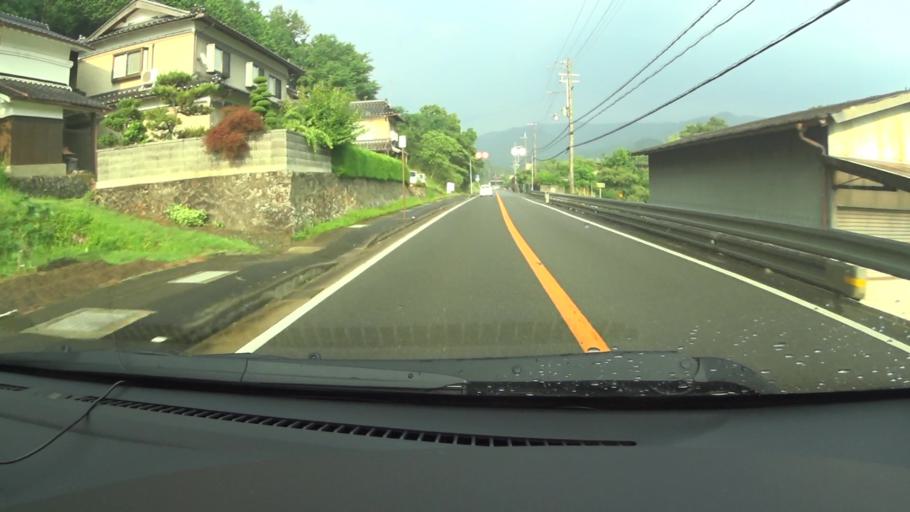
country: JP
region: Kyoto
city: Ayabe
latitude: 35.2908
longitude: 135.2773
